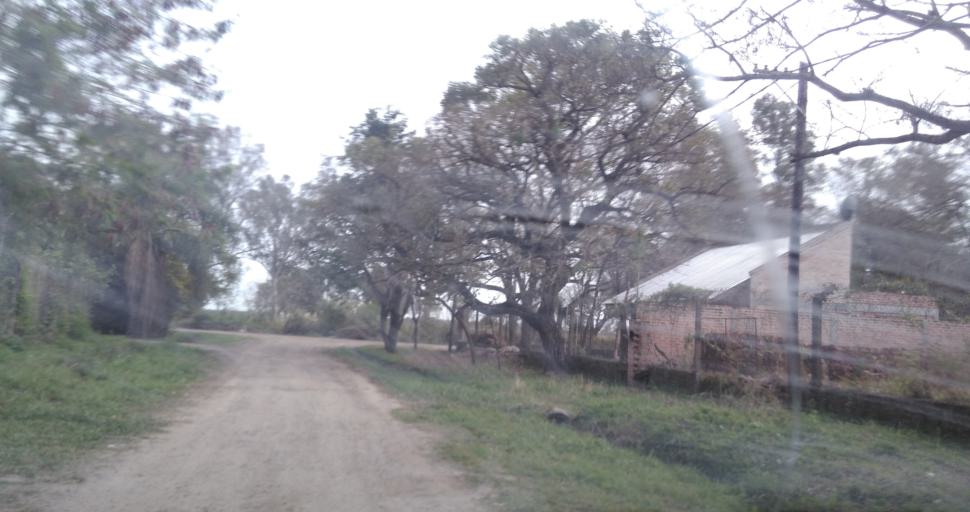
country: AR
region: Chaco
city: Fontana
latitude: -27.4436
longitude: -59.0351
